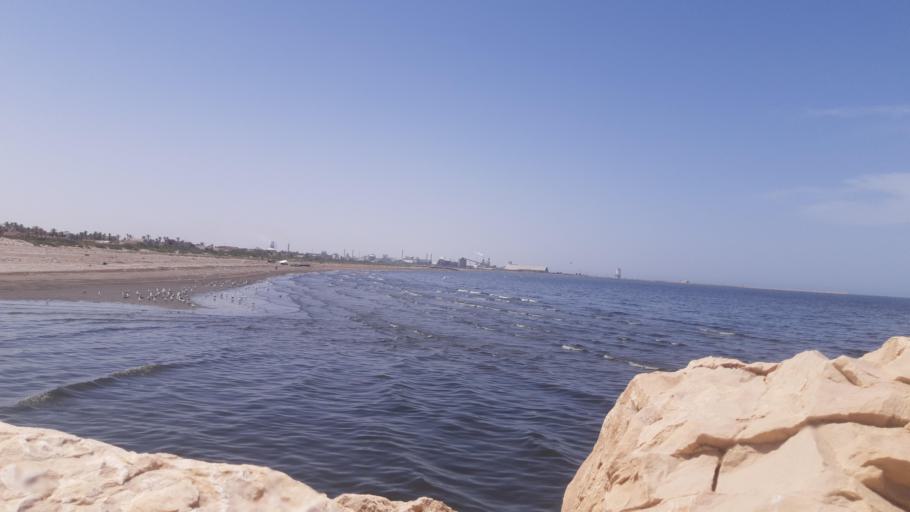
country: TN
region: Qabis
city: Gabes
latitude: 33.8959
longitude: 10.1148
